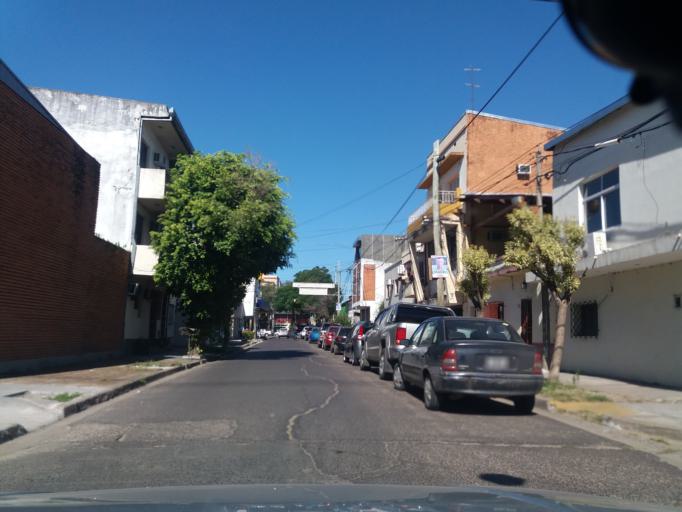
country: AR
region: Corrientes
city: Corrientes
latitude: -27.4739
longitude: -58.8421
